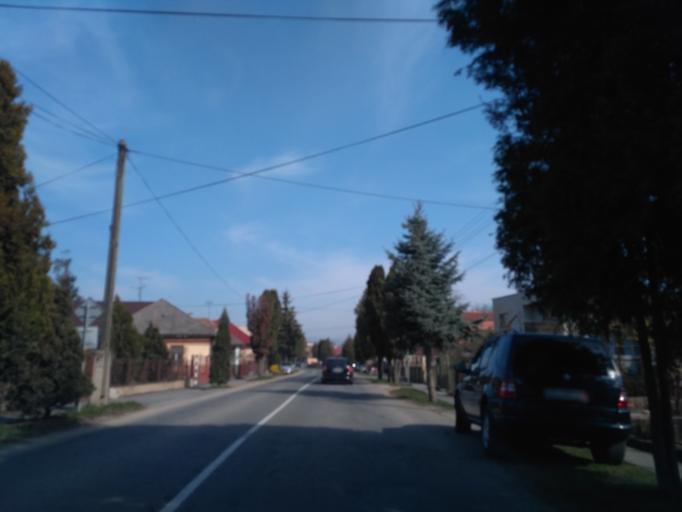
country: SK
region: Kosicky
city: Moldava nad Bodvou
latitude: 48.5937
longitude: 21.0221
